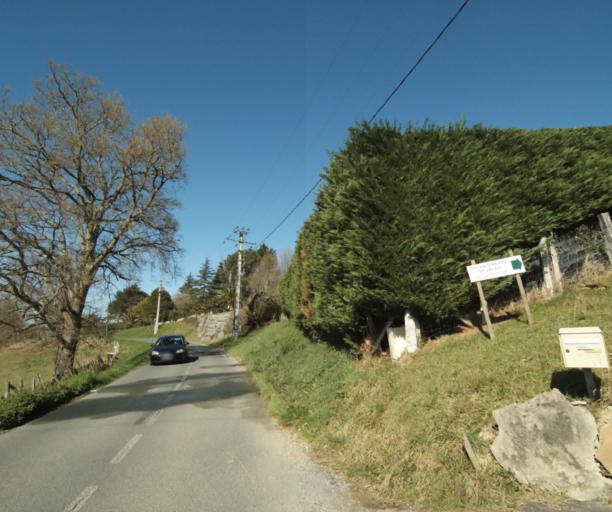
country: FR
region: Aquitaine
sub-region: Departement des Pyrenees-Atlantiques
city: Urrugne
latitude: 43.3611
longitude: -1.6817
